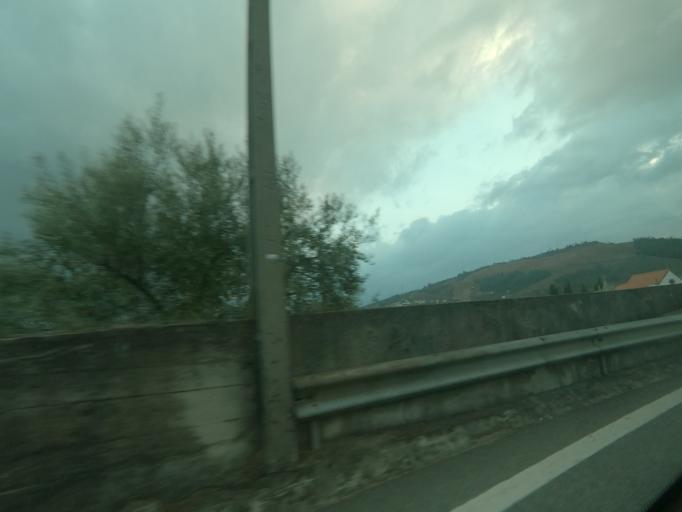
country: PT
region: Vila Real
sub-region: Mesao Frio
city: Mesao Frio
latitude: 41.1564
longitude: -7.8861
